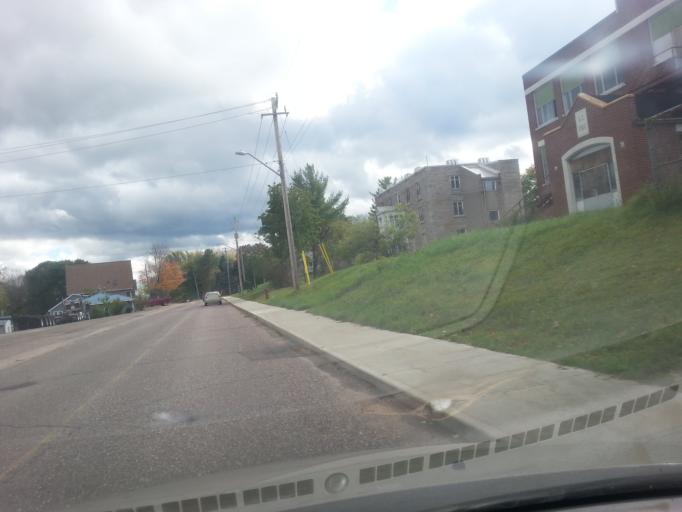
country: CA
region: Ontario
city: Pembroke
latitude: 45.5351
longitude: -77.0961
